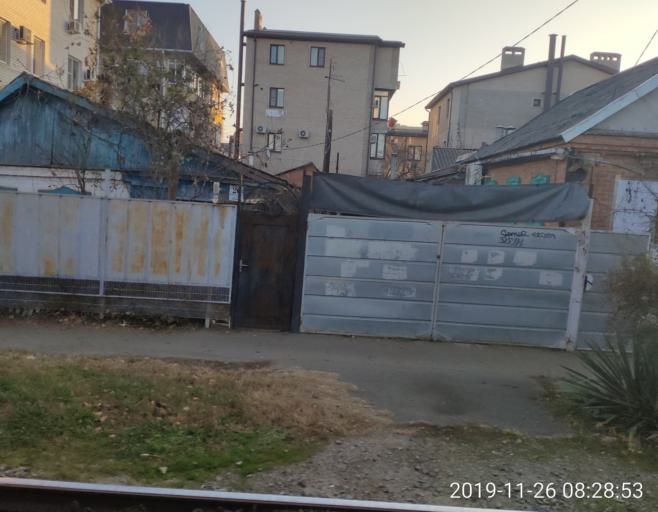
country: RU
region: Krasnodarskiy
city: Krasnodar
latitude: 45.0535
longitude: 39.0028
